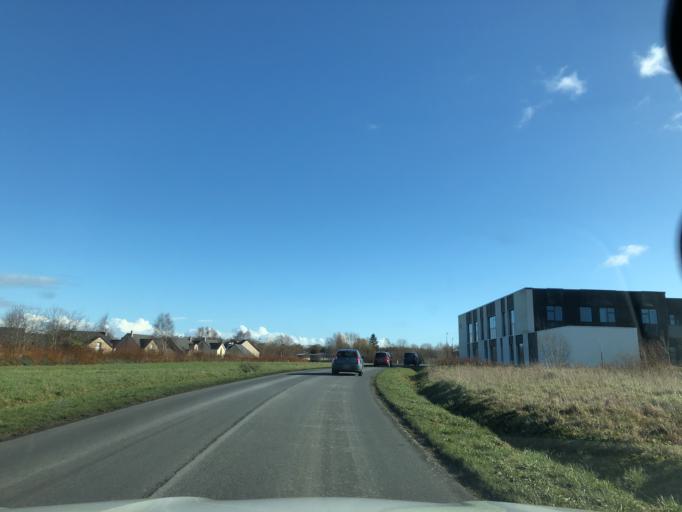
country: FR
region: Lower Normandy
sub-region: Departement du Calvados
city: Epron
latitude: 49.2198
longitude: -0.3572
